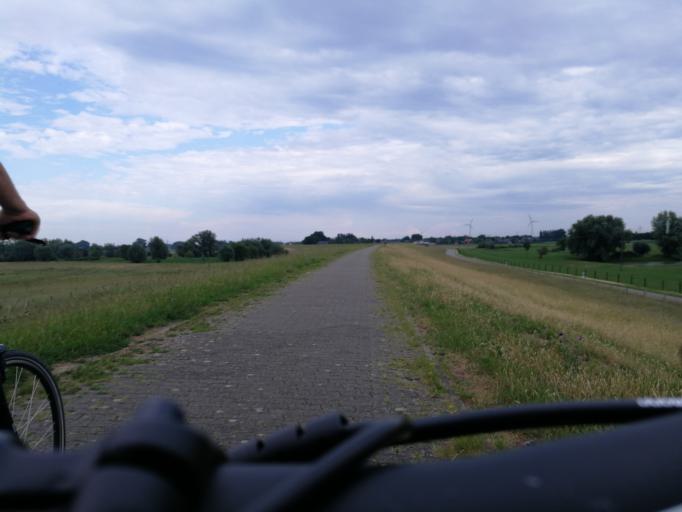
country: DE
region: North Rhine-Westphalia
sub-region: Regierungsbezirk Dusseldorf
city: Kleve
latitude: 51.8292
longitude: 6.1252
